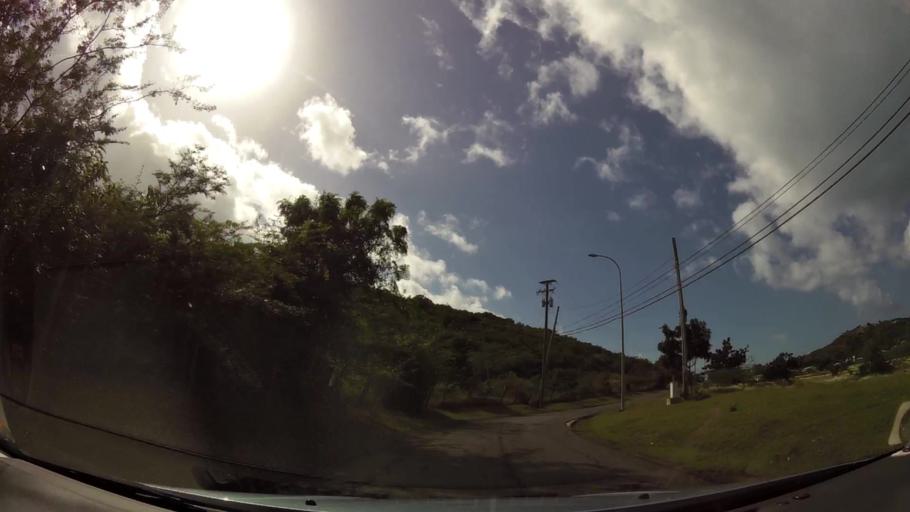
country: AG
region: Saint John
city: Saint John's
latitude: 17.1164
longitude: -61.8796
